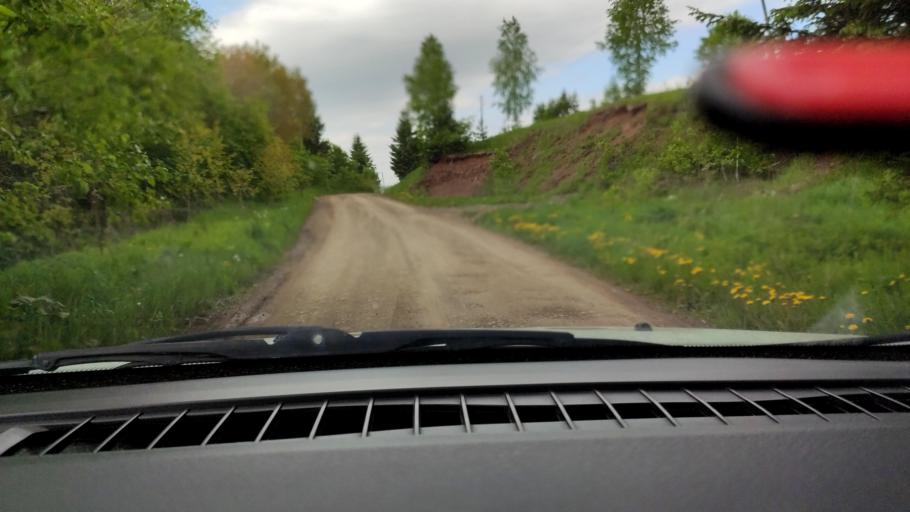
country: RU
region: Perm
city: Bershet'
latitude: 57.7236
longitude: 56.3963
